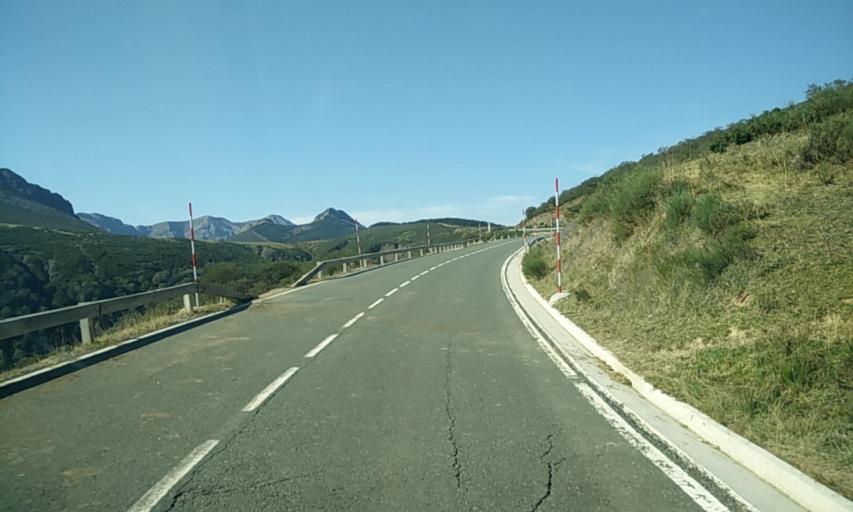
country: ES
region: Cantabria
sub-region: Provincia de Cantabria
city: Camaleno
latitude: 43.0700
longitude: -4.7532
